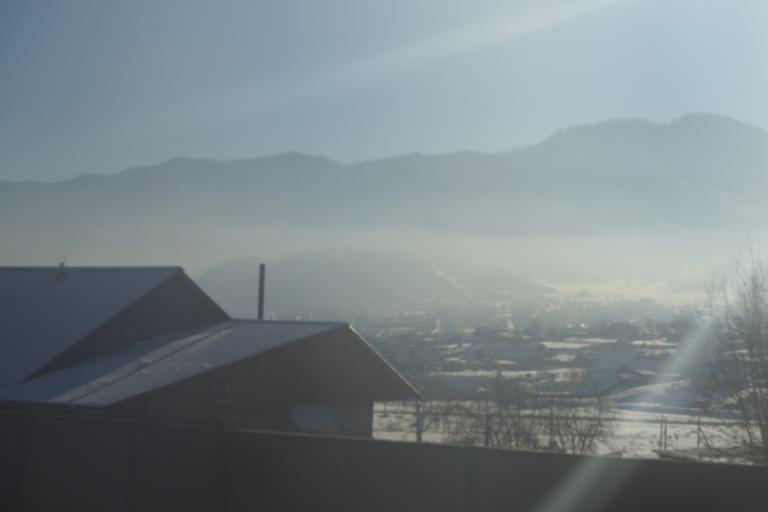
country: RU
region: Altay
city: Onguday
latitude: 50.7608
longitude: 86.1193
